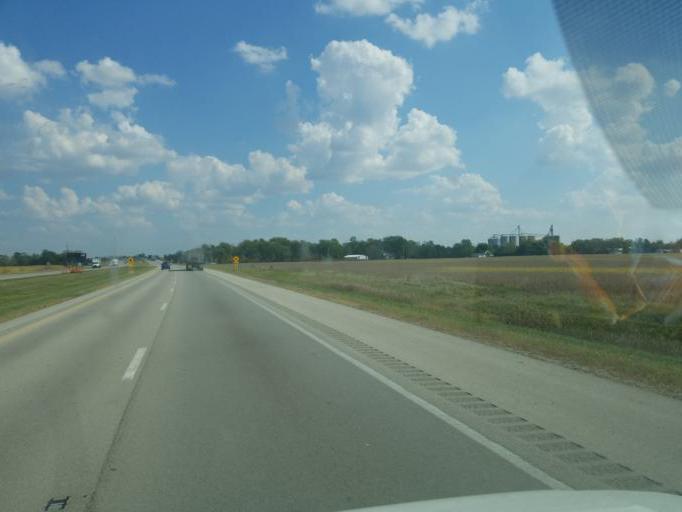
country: US
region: Ohio
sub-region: Van Wert County
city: Van Wert
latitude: 40.8872
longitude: -84.5954
